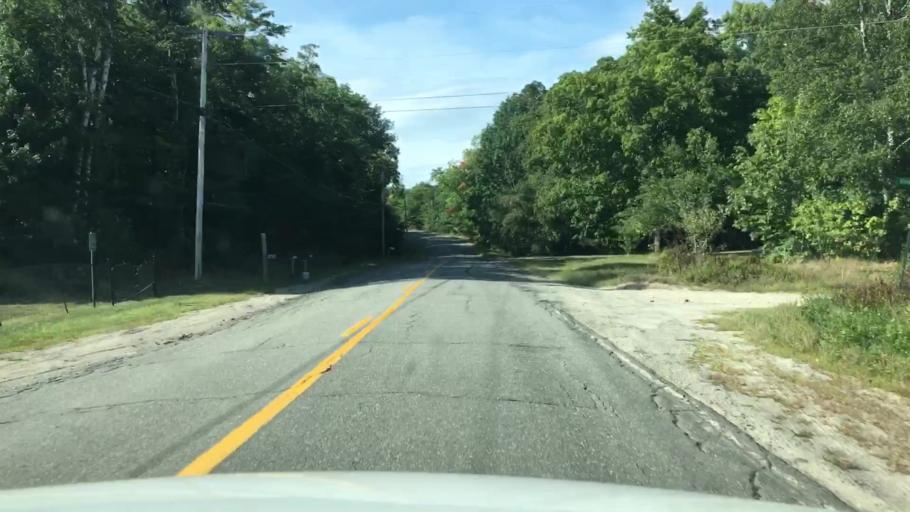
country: US
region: Maine
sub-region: Penobscot County
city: Enfield
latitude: 45.2230
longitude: -68.5379
